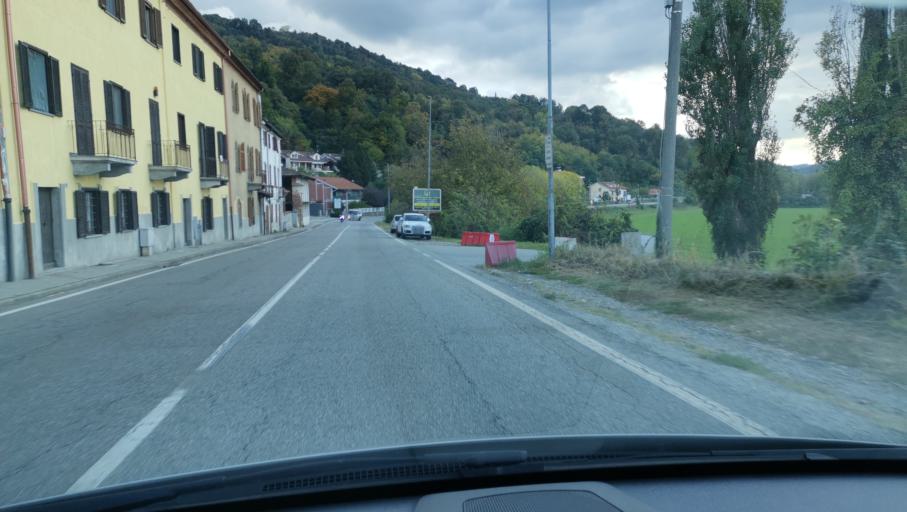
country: IT
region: Piedmont
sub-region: Provincia di Torino
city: Piana San Raffaele
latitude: 45.1674
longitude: 7.8573
